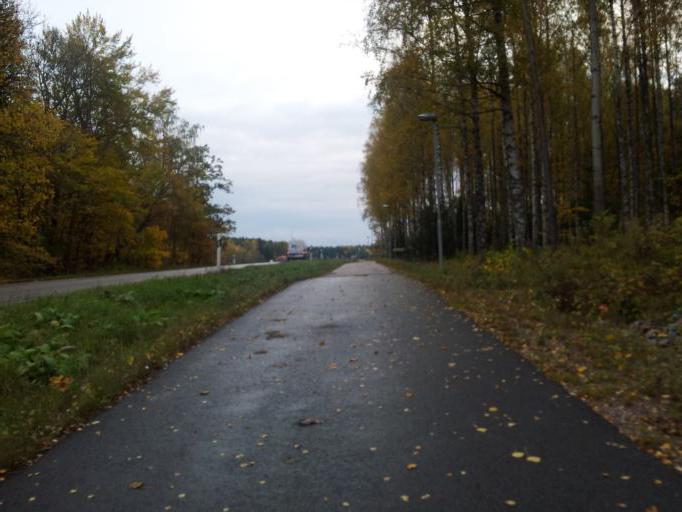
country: SE
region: Uppsala
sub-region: Uppsala Kommun
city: Storvreta
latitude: 59.9044
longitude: 17.7170
